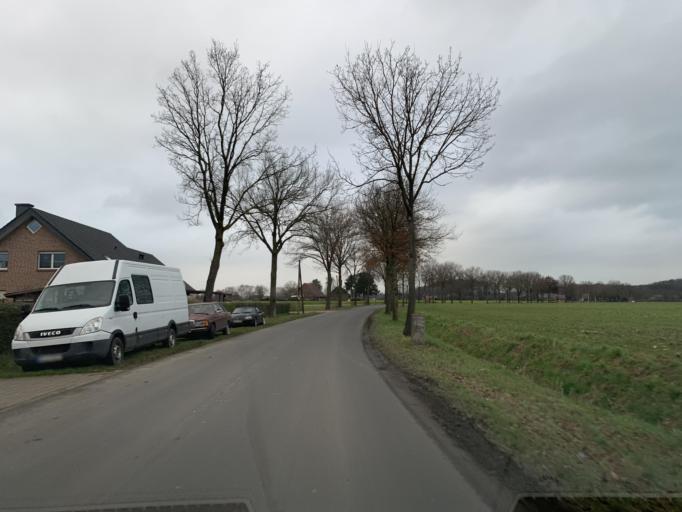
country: DE
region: North Rhine-Westphalia
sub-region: Regierungsbezirk Munster
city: Muenster
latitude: 51.9339
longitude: 7.5393
